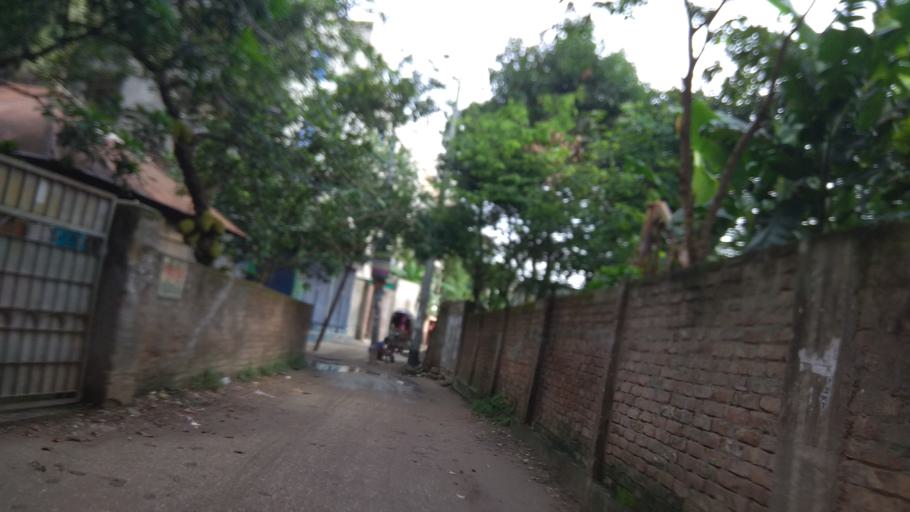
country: BD
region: Dhaka
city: Azimpur
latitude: 23.7933
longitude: 90.3800
